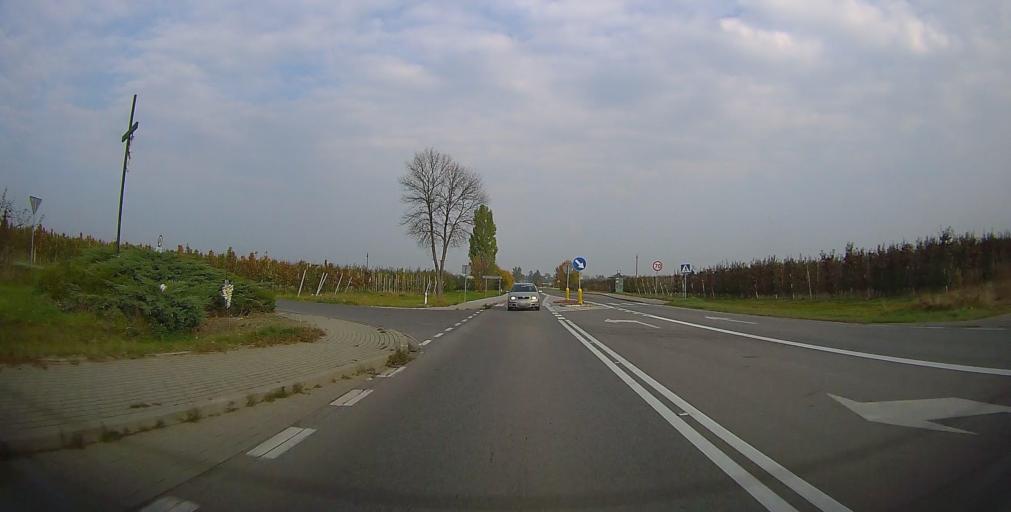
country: PL
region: Masovian Voivodeship
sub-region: Powiat grojecki
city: Bledow
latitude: 51.7636
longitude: 20.7672
